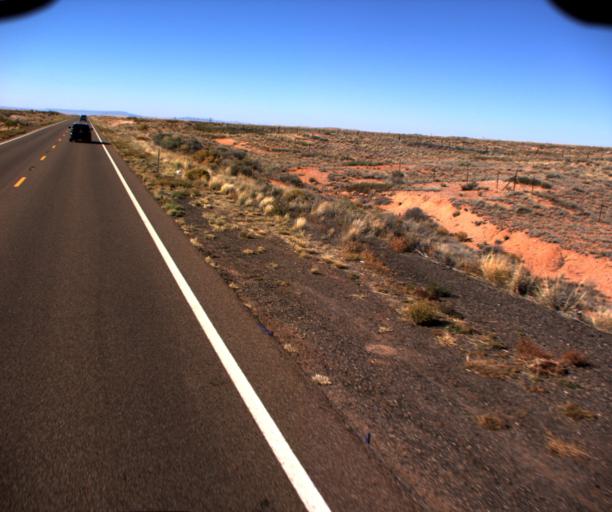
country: US
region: Arizona
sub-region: Navajo County
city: Winslow
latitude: 35.1333
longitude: -110.4931
